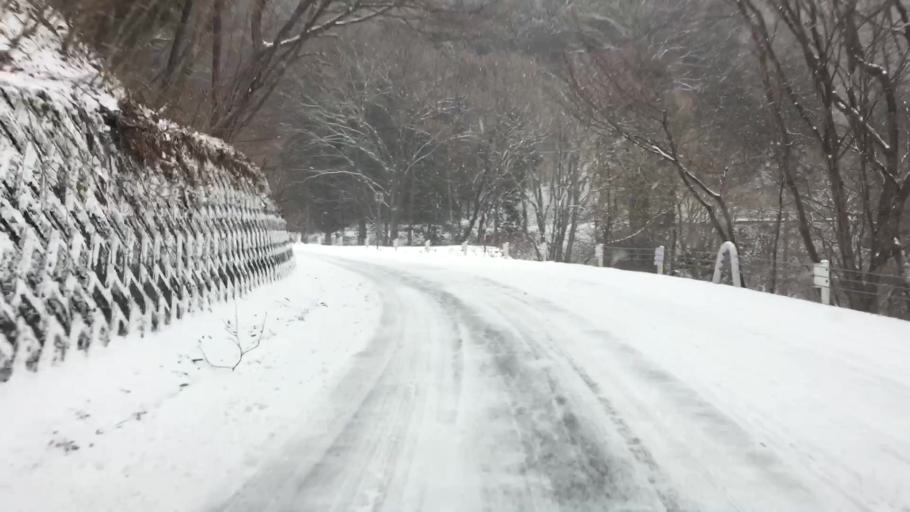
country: JP
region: Tochigi
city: Nikko
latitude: 36.8781
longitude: 139.7207
